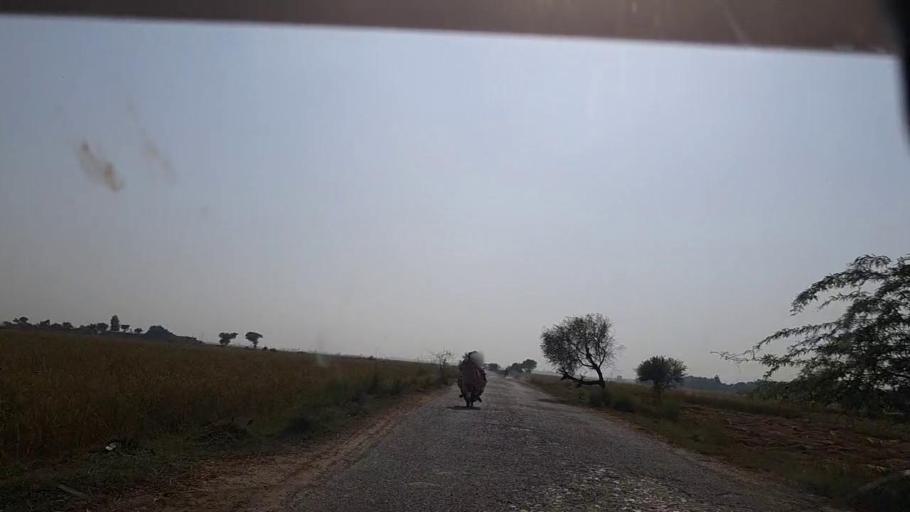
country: PK
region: Sindh
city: Shikarpur
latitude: 28.0928
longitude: 68.6083
